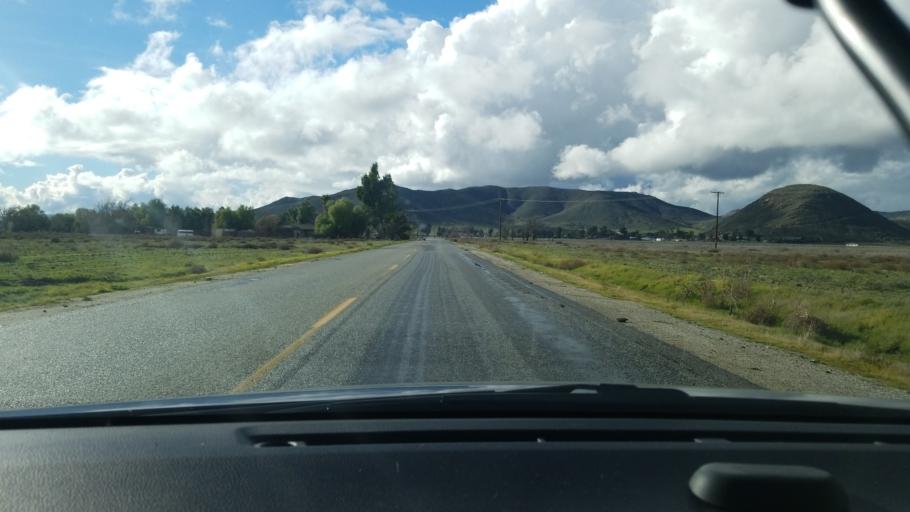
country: US
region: California
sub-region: Riverside County
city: Green Acres
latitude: 33.7292
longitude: -117.0359
